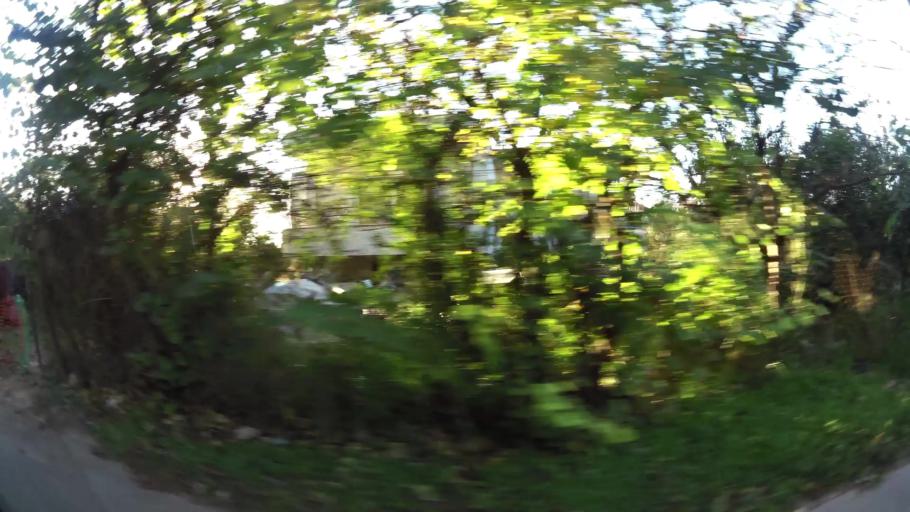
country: GR
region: Attica
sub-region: Nomarchia Anatolikis Attikis
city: Kryoneri
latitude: 38.1265
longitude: 23.8303
